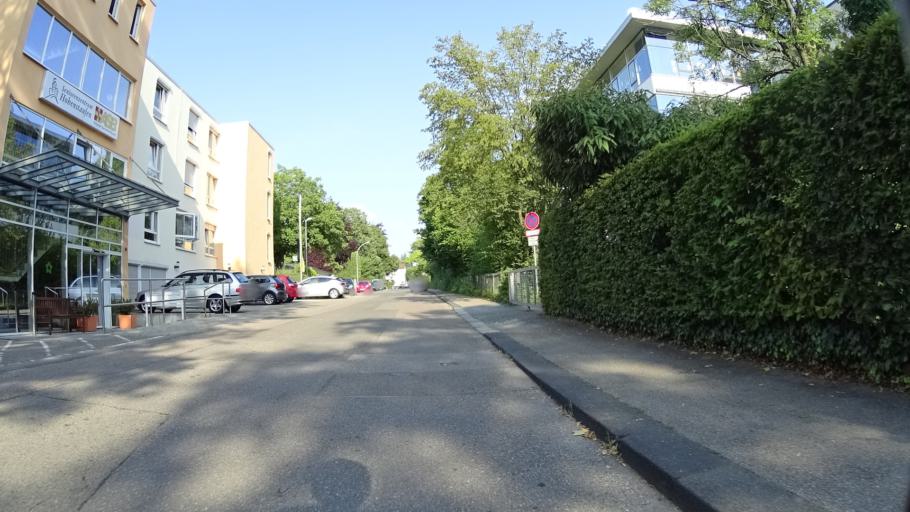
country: DE
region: Baden-Wuerttemberg
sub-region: Regierungsbezirk Stuttgart
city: Goeppingen
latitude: 48.7048
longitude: 9.6686
